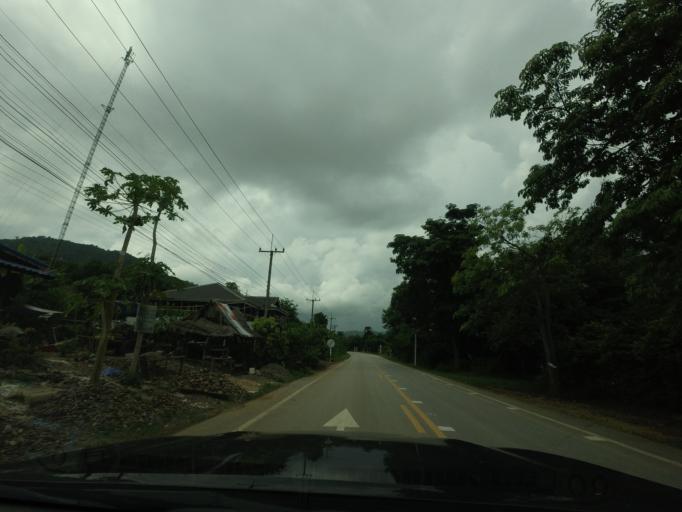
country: TH
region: Loei
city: Pak Chom
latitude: 18.0592
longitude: 101.8000
